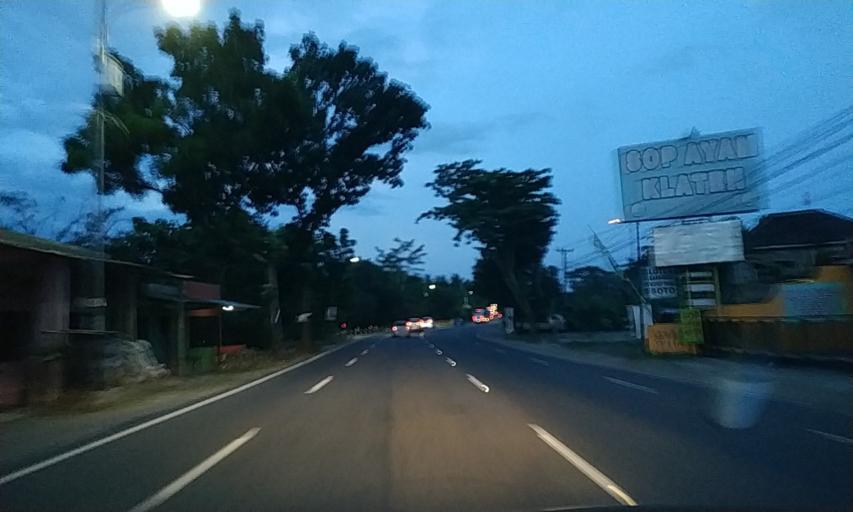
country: ID
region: Daerah Istimewa Yogyakarta
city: Godean
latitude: -7.8155
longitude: 110.2517
